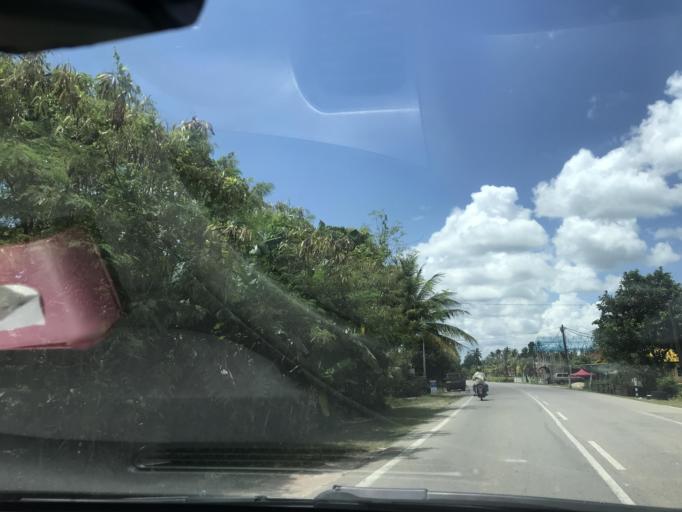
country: MY
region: Kelantan
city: Tumpat
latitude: 6.2060
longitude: 102.1173
